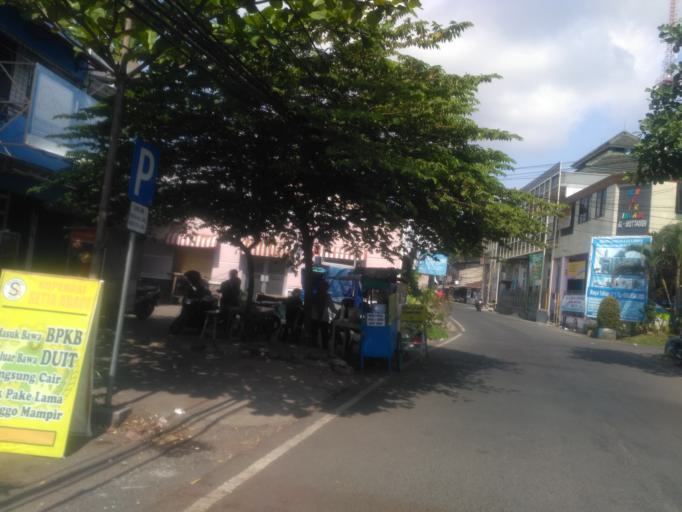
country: ID
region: East Java
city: Malang
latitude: -7.9410
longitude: 112.6387
